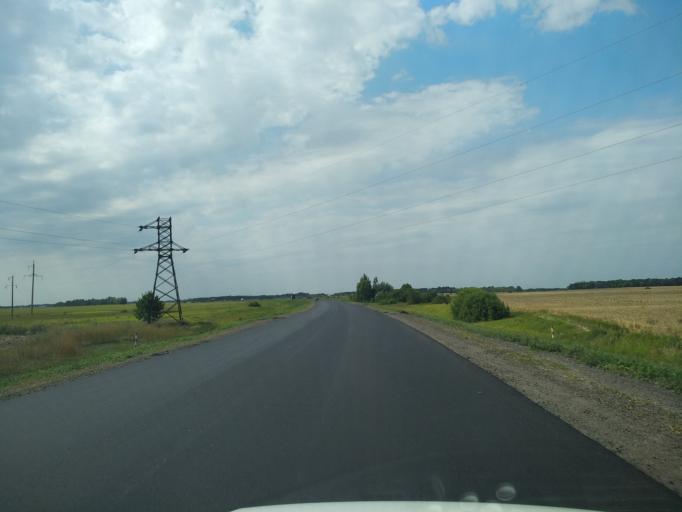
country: RU
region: Voronezj
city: Pereleshino
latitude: 51.7825
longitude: 40.1394
